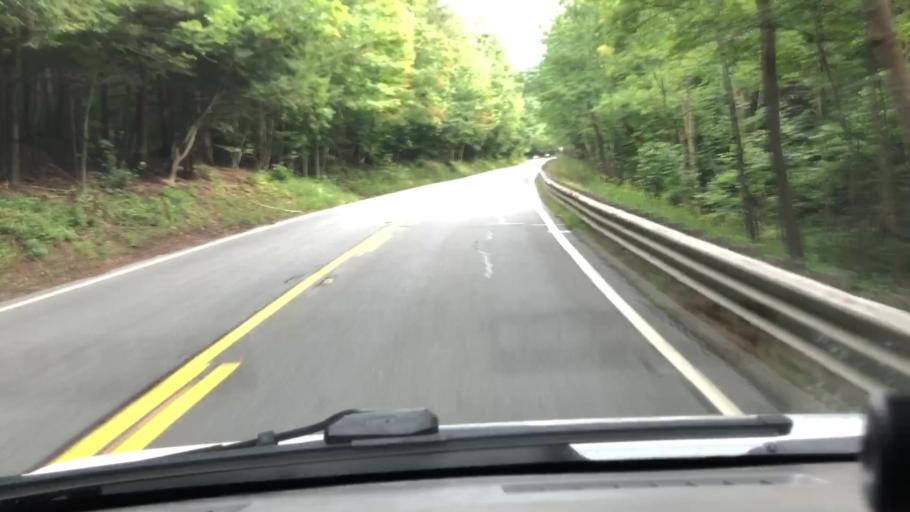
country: US
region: Massachusetts
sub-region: Berkshire County
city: North Adams
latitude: 42.6496
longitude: -72.9948
